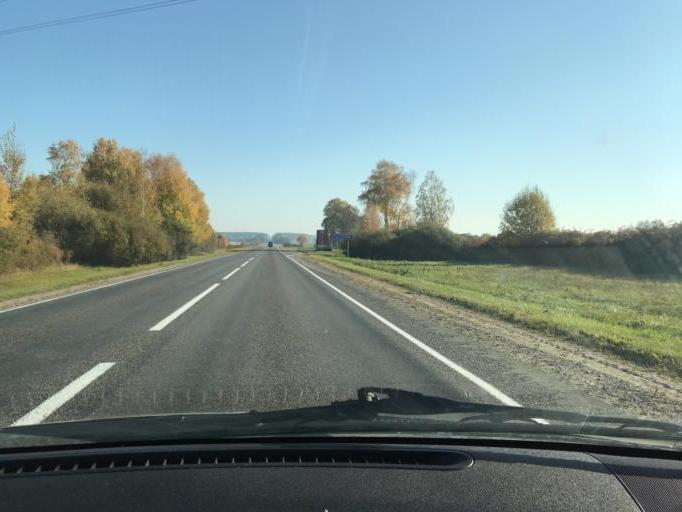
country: BY
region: Brest
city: Baranovichi
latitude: 52.9319
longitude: 26.0395
